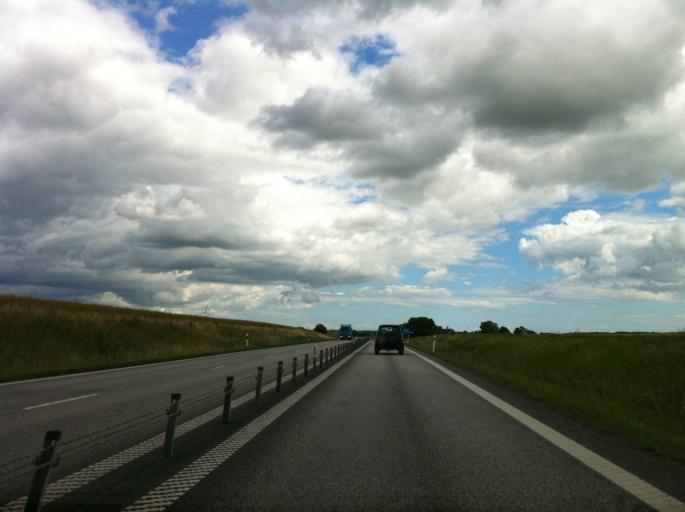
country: SE
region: Skane
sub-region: Trelleborgs Kommun
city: Anderslov
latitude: 55.5002
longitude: 13.4051
